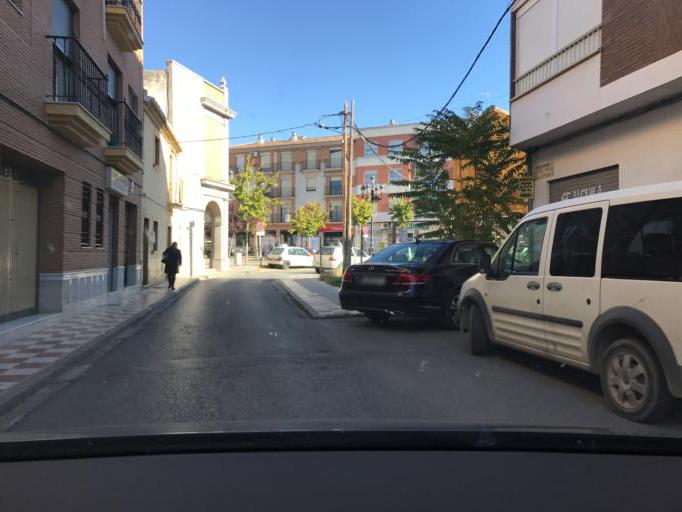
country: ES
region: Andalusia
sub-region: Provincia de Granada
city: Albolote
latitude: 37.2302
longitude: -3.6574
